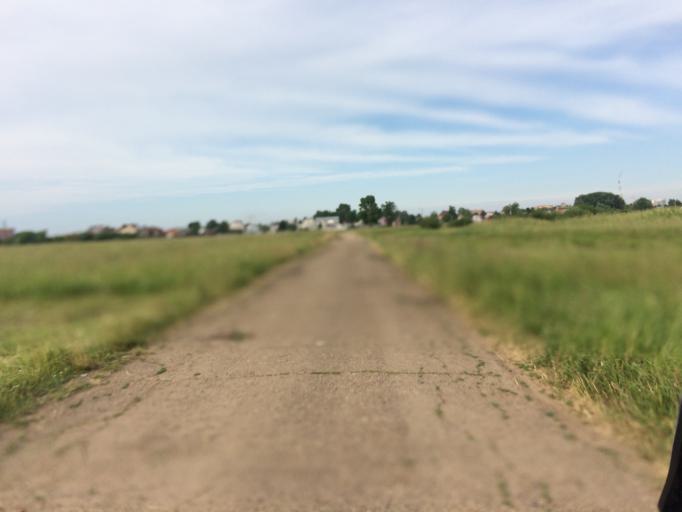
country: RU
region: Mariy-El
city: Yoshkar-Ola
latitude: 56.6550
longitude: 47.9218
